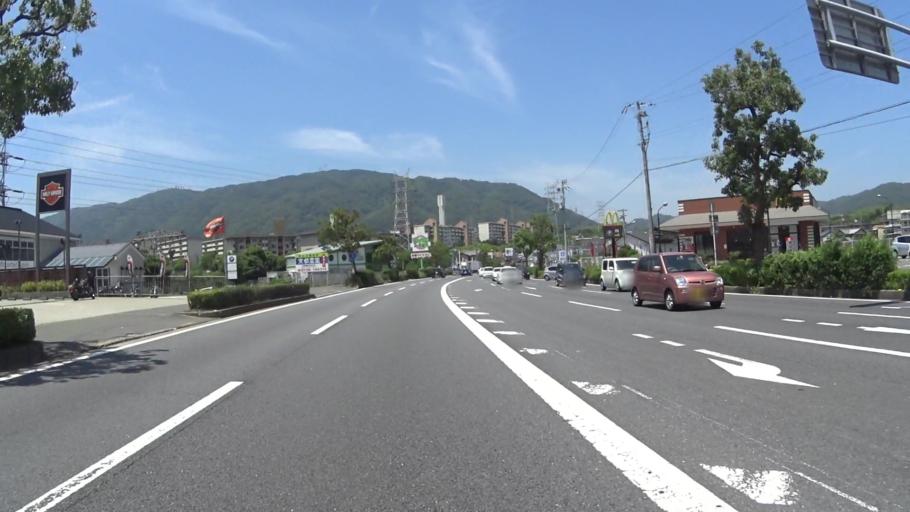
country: JP
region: Kyoto
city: Muko
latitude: 34.9708
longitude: 135.6744
